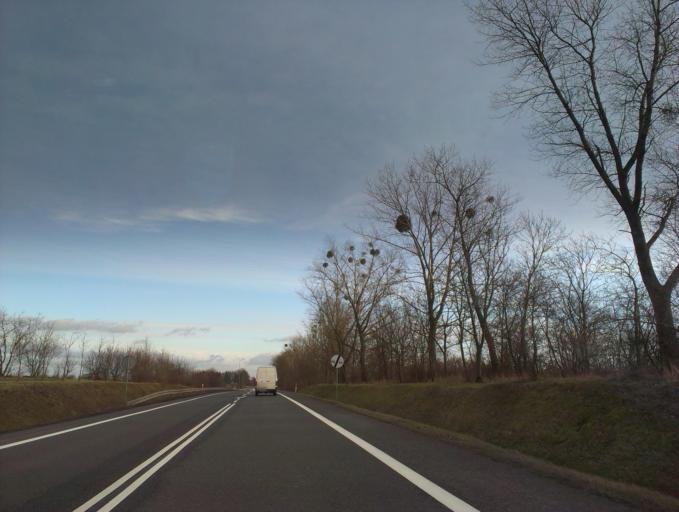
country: PL
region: Kujawsko-Pomorskie
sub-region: Powiat torunski
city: Czernikowo
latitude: 52.9333
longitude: 19.0057
